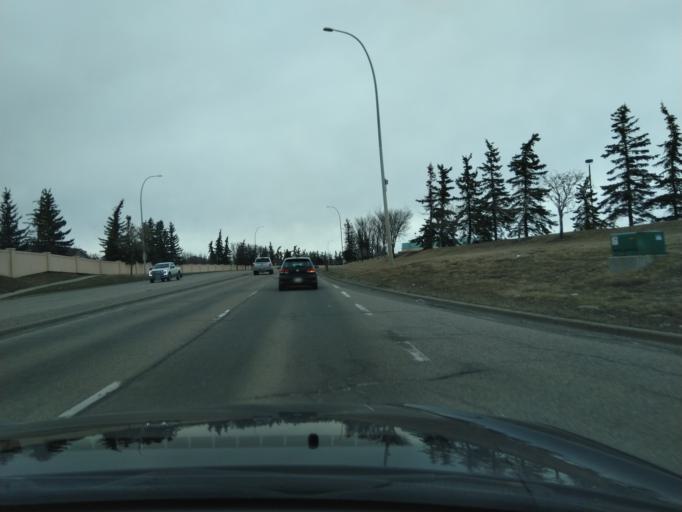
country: CA
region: Alberta
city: Calgary
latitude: 51.1378
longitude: -114.1633
